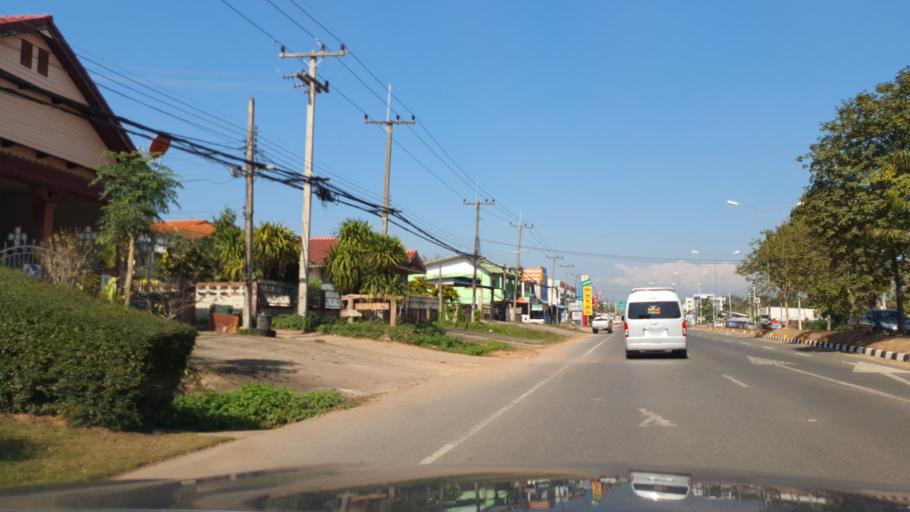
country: TH
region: Nan
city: Pua
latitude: 19.1676
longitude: 100.9233
